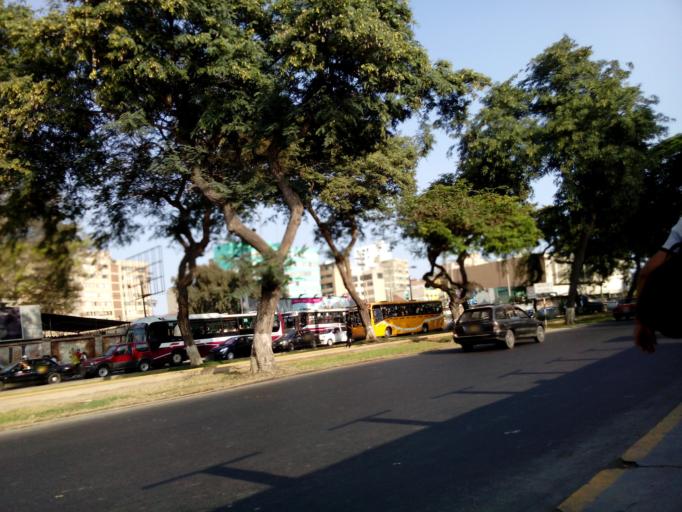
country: PE
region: Lima
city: Lima
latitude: -12.0653
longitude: -77.0392
